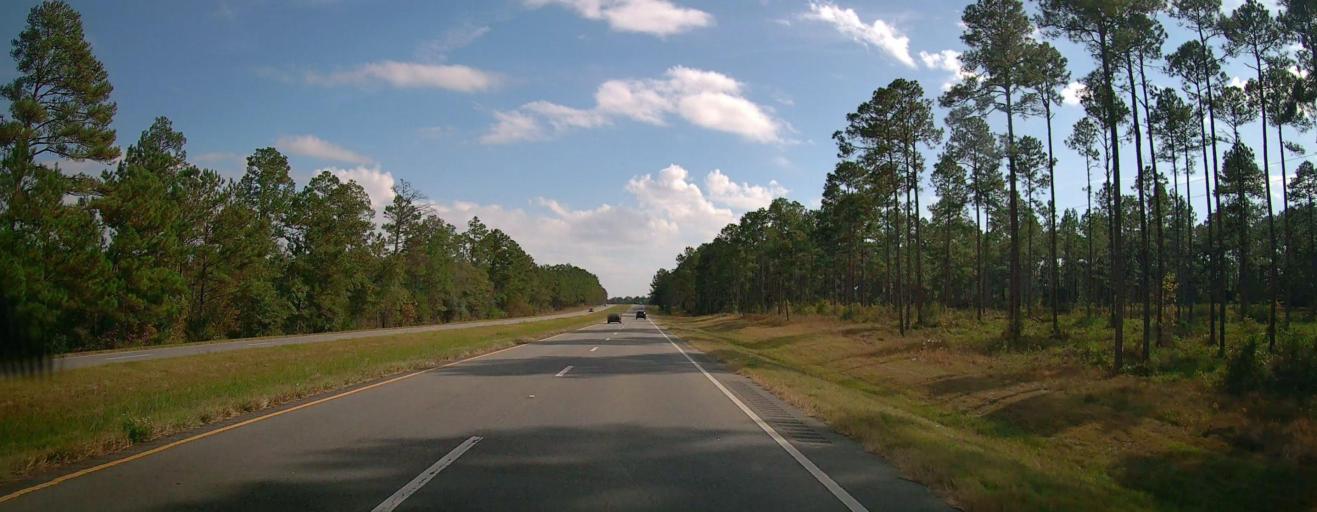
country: US
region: Georgia
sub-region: Thomas County
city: Thomasville
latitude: 30.9573
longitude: -84.0279
